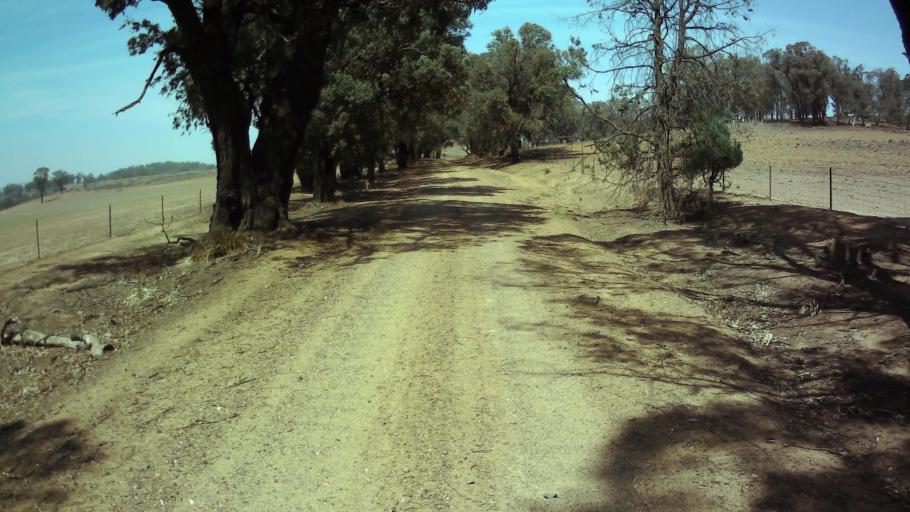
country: AU
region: New South Wales
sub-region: Weddin
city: Grenfell
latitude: -33.8971
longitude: 148.1340
